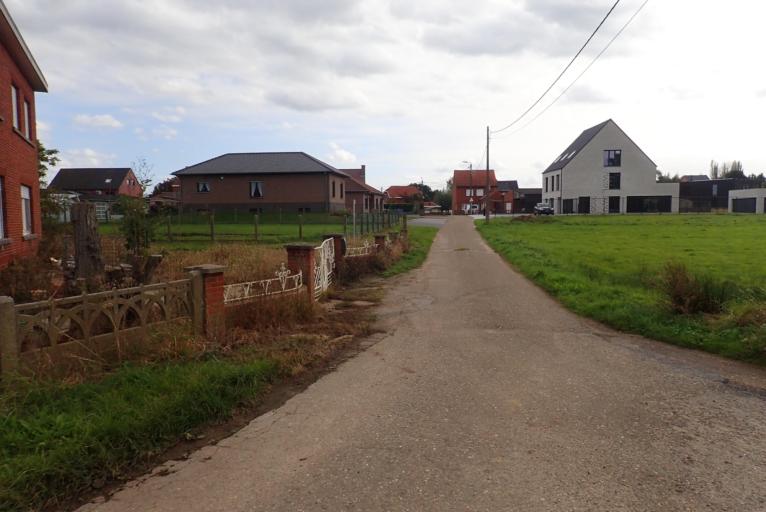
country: BE
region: Flanders
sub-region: Provincie Vlaams-Brabant
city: Aarschot
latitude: 50.9809
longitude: 4.8991
